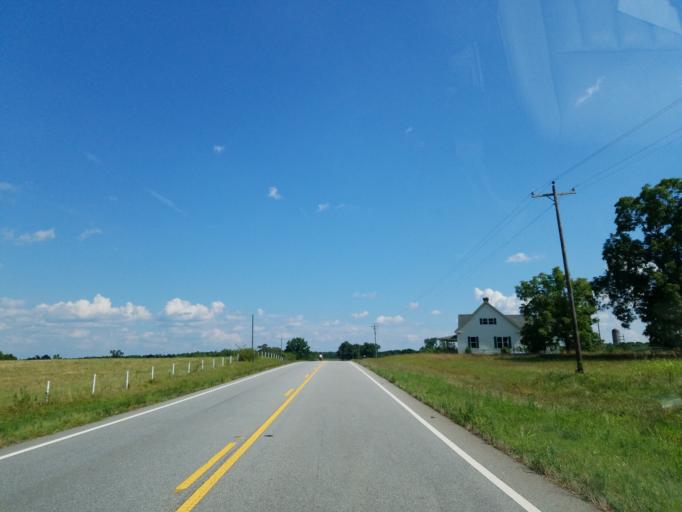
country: US
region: Georgia
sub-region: Lamar County
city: Barnesville
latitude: 32.9389
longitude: -84.0881
